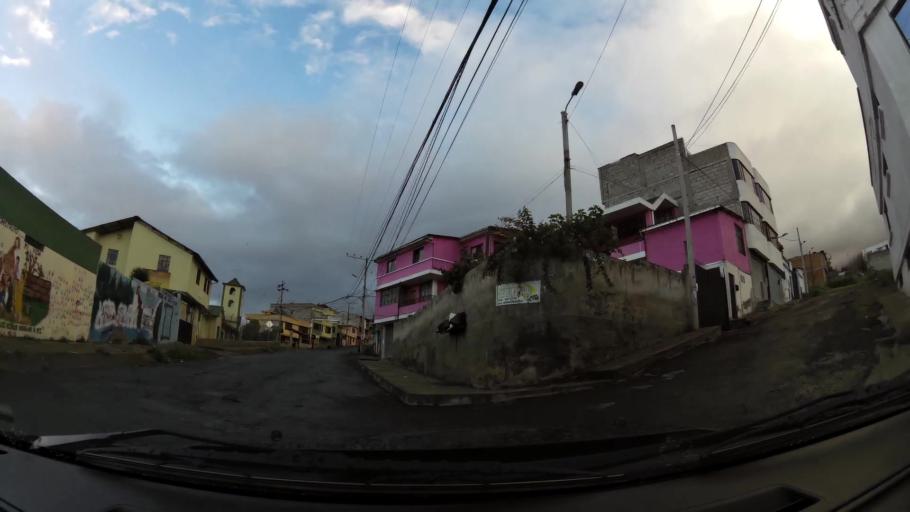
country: EC
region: Pichincha
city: Quito
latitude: -0.1142
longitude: -78.5088
